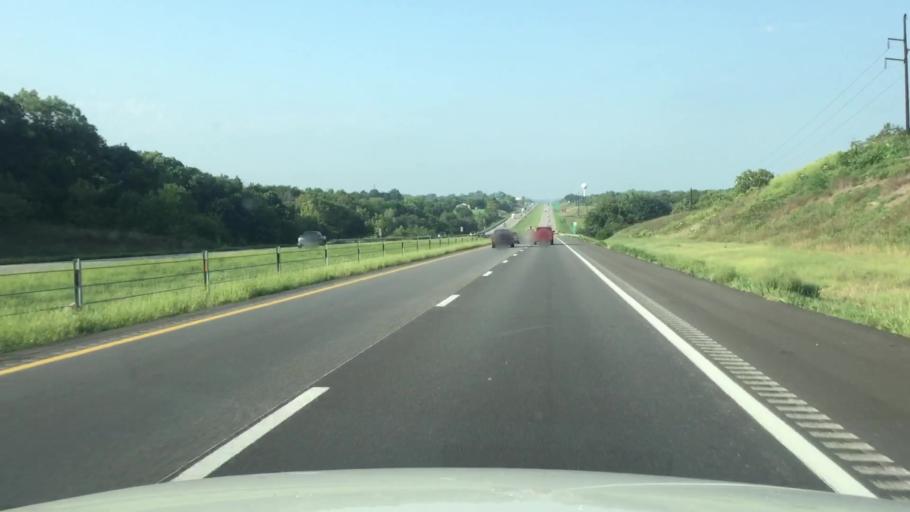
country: US
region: Missouri
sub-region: Clay County
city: Kearney
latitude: 39.3428
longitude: -94.3855
